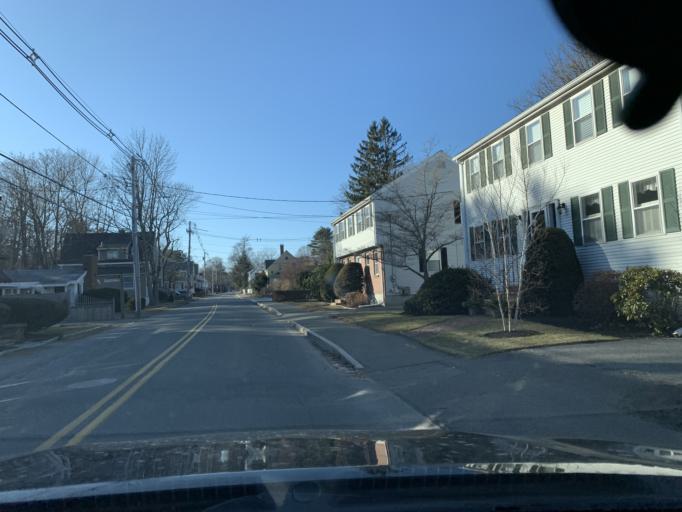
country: US
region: Massachusetts
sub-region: Essex County
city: Essex
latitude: 42.5837
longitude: -70.7729
